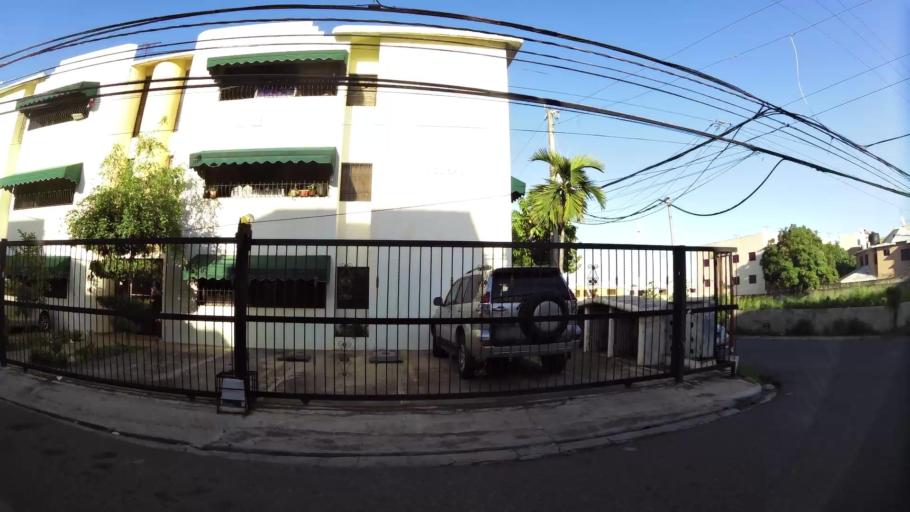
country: DO
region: Nacional
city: Santo Domingo
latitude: 18.4900
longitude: -69.9738
